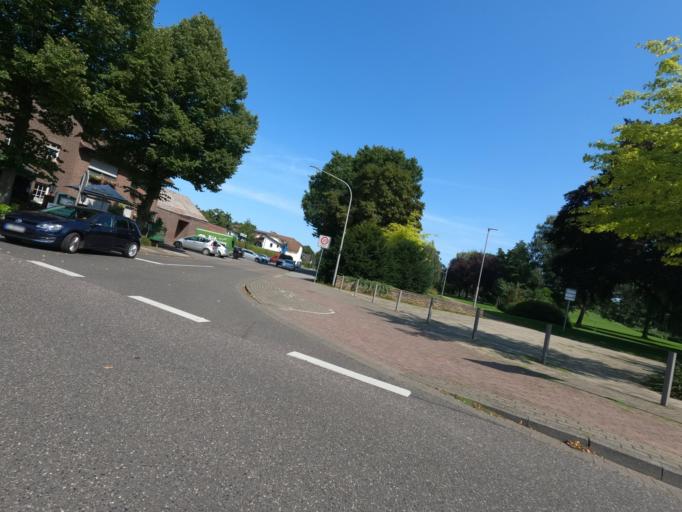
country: DE
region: North Rhine-Westphalia
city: Baesweiler
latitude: 50.9232
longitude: 6.1991
